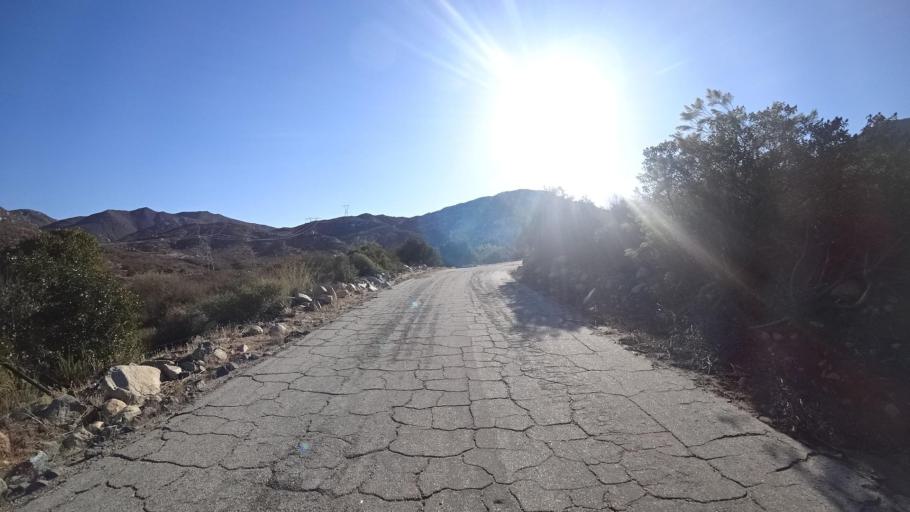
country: MX
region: Baja California
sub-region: Tecate
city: Lomas de Santa Anita
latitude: 32.6041
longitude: -116.6857
